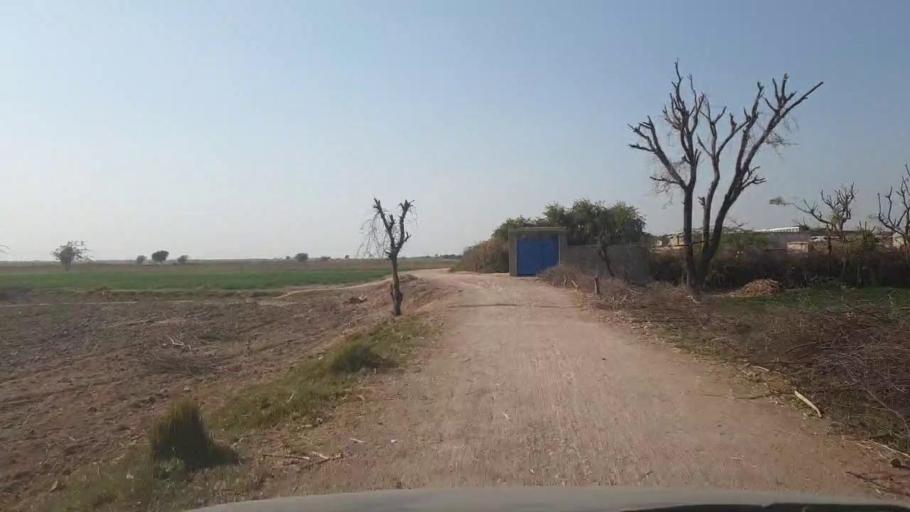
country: PK
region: Sindh
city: Chambar
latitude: 25.3190
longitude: 68.8404
